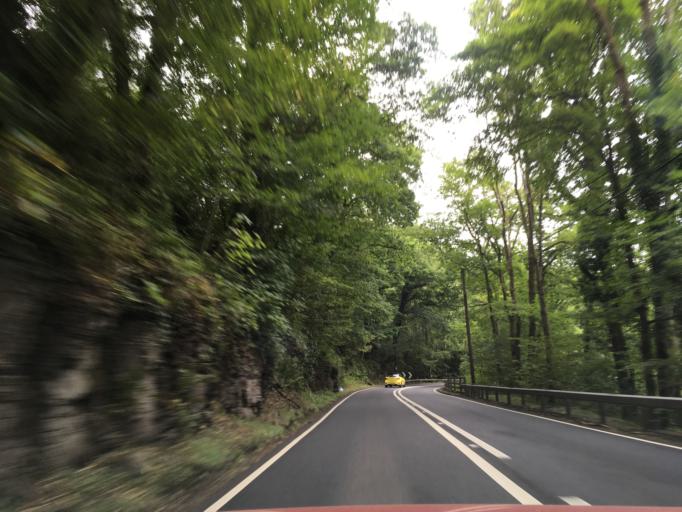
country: GB
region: Wales
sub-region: Carmarthenshire
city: Llandovery
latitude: 51.9941
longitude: -3.7395
